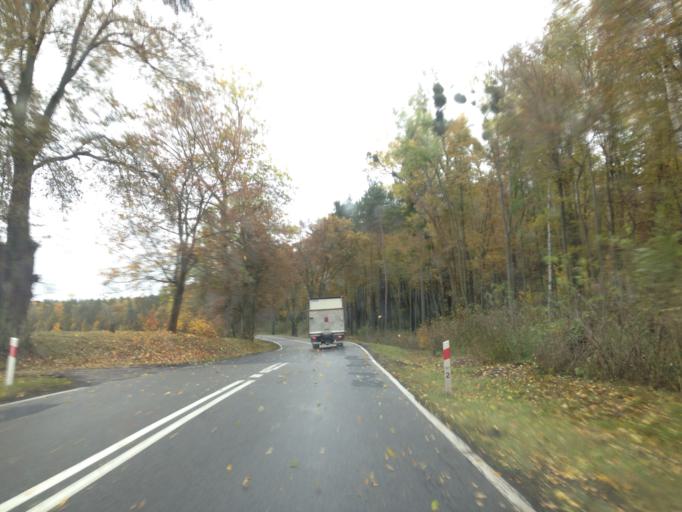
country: PL
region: Pomeranian Voivodeship
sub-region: Powiat kwidzynski
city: Ryjewo
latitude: 53.8486
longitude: 18.9993
